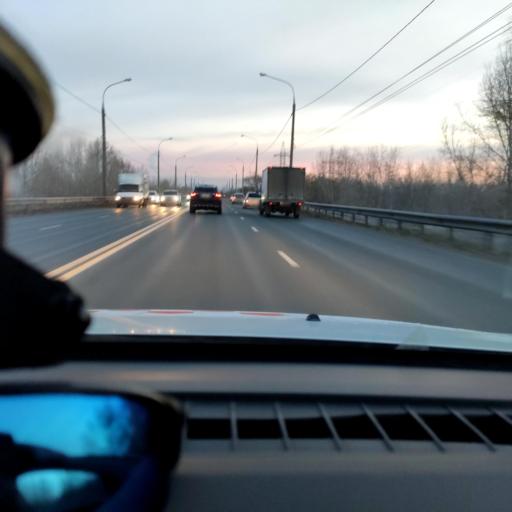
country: RU
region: Samara
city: Samara
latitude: 53.1531
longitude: 50.1883
